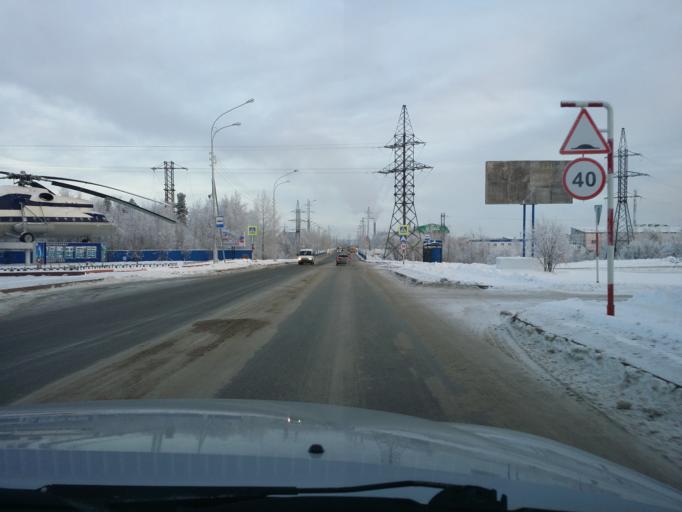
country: RU
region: Khanty-Mansiyskiy Avtonomnyy Okrug
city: Nizhnevartovsk
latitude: 60.9502
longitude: 76.5010
